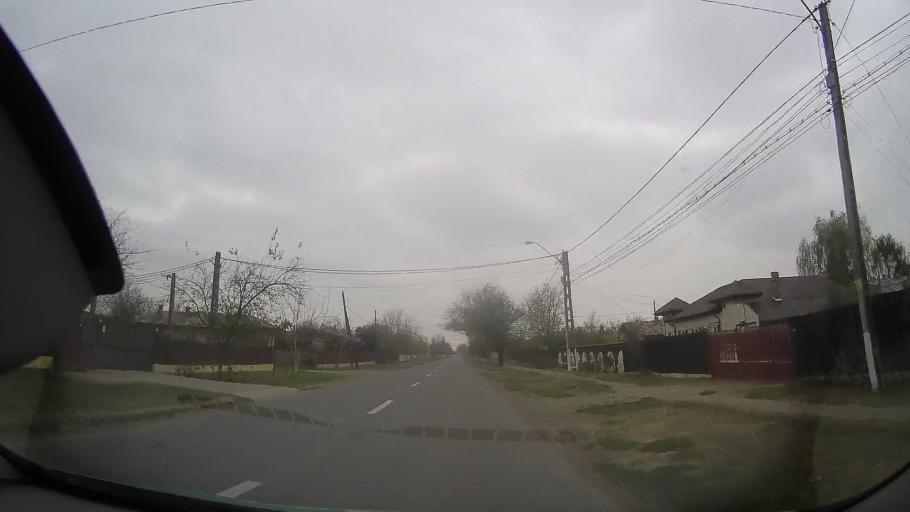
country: RO
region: Ialomita
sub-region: Comuna Manasia
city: Manasia
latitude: 44.7129
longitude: 26.6776
